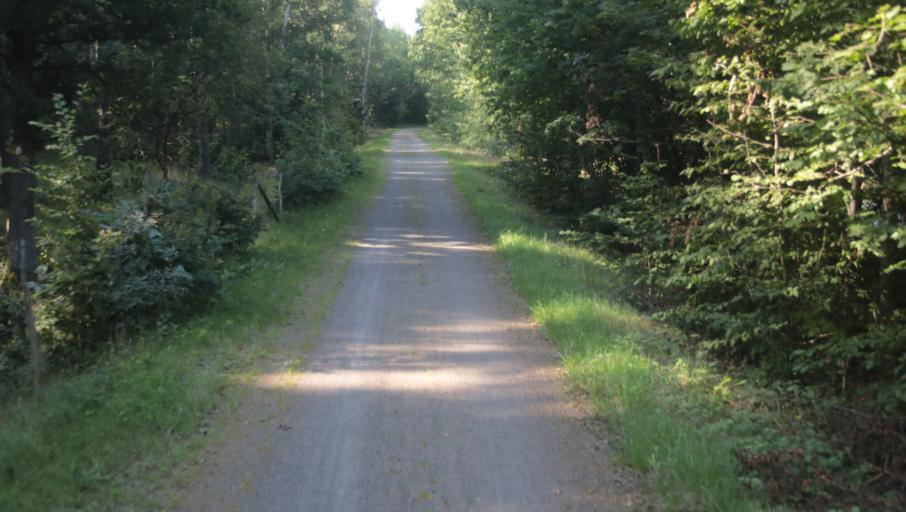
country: SE
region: Blekinge
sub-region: Karlshamns Kommun
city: Svangsta
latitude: 56.2811
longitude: 14.7549
